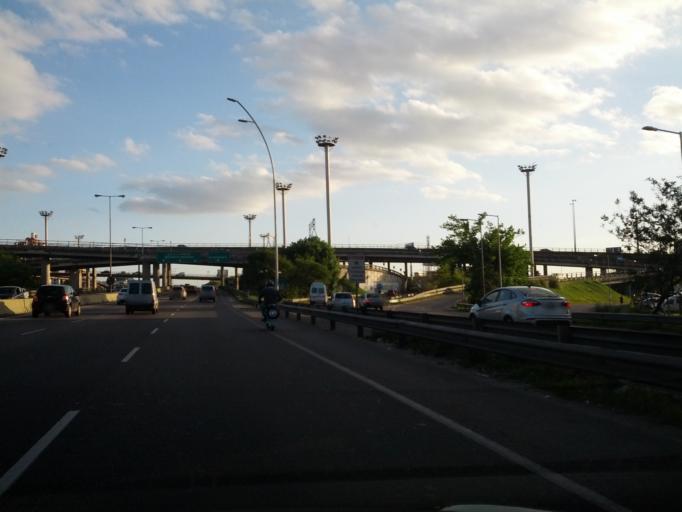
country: AR
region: Buenos Aires
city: Caseros
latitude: -34.6329
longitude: -58.5301
